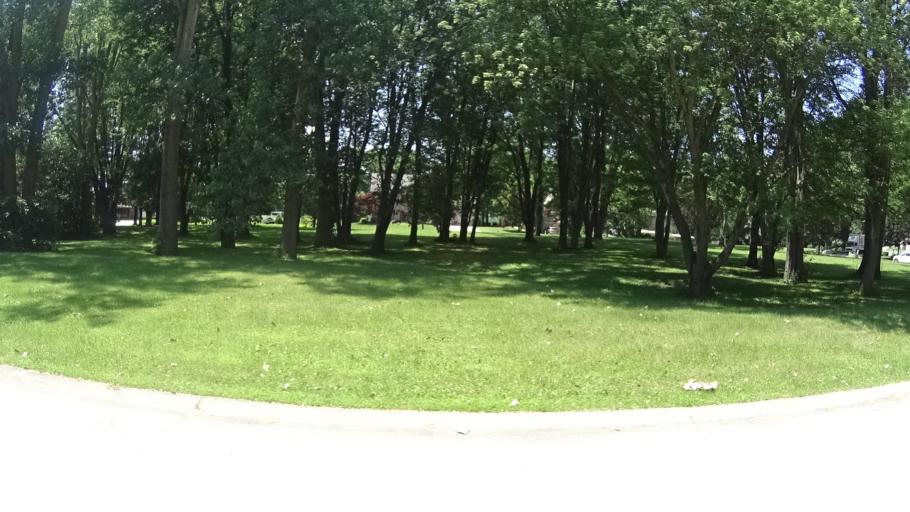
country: US
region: Ohio
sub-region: Erie County
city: Sandusky
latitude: 41.4118
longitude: -82.6371
